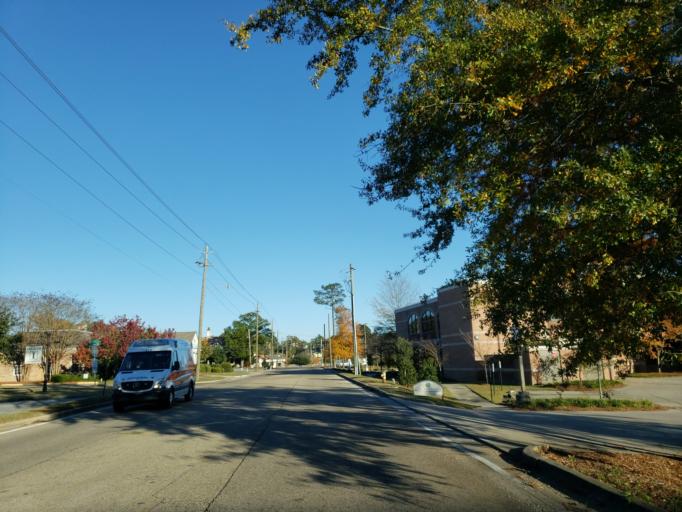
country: US
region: Mississippi
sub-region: Lamar County
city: West Hattiesburg
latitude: 31.3211
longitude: -89.3330
